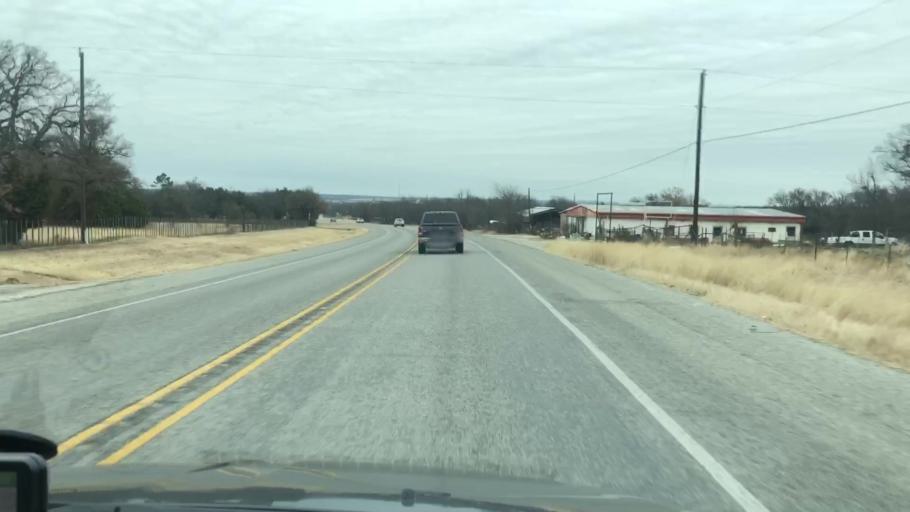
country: US
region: Texas
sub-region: Palo Pinto County
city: Mineral Wells
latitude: 32.8841
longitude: -98.0894
